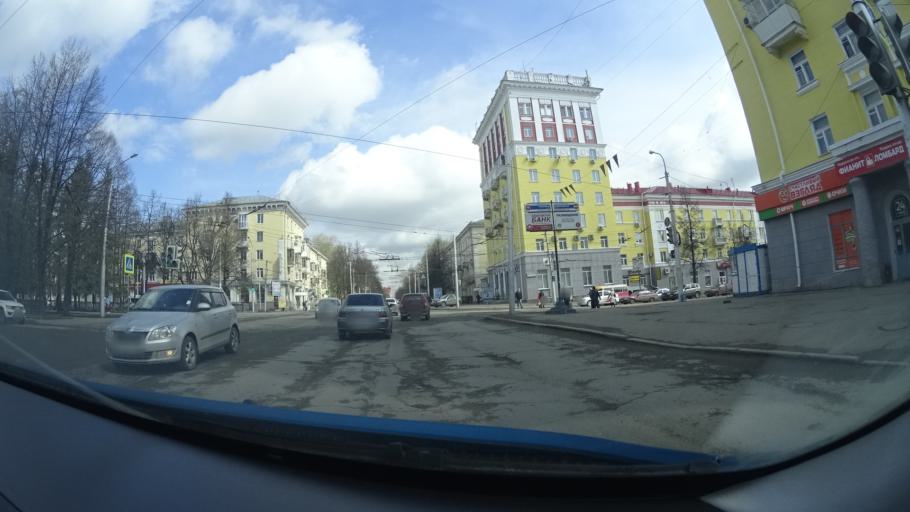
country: RU
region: Bashkortostan
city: Ufa
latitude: 54.8172
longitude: 56.0744
